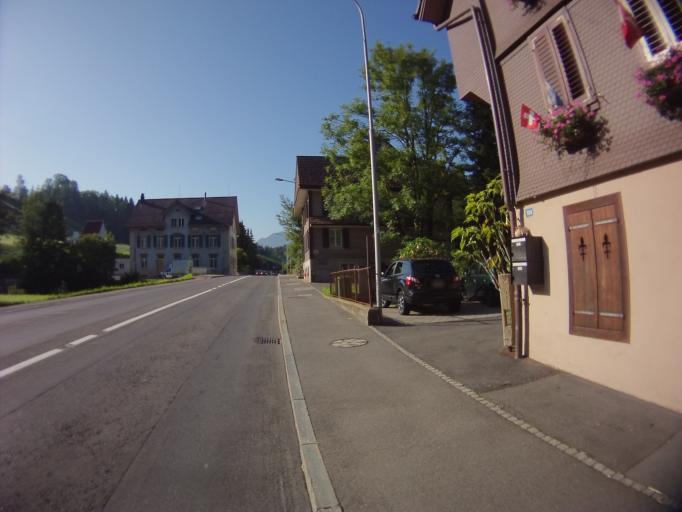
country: CH
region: Zug
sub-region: Zug
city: Unterageri
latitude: 47.1537
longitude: 8.5622
